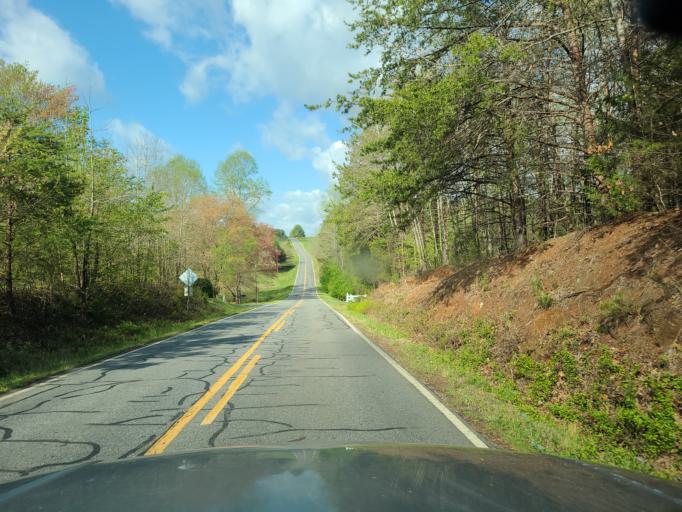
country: US
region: North Carolina
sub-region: Rutherford County
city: Forest City
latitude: 35.4360
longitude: -81.8348
